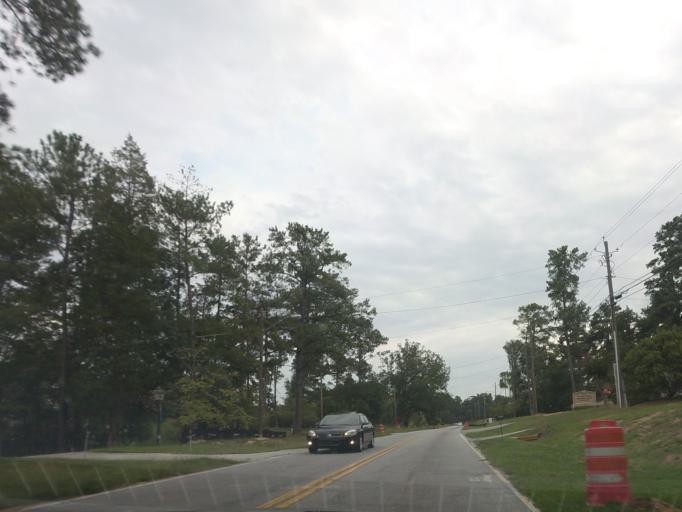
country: US
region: Georgia
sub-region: Bibb County
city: Macon
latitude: 32.8770
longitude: -83.6932
